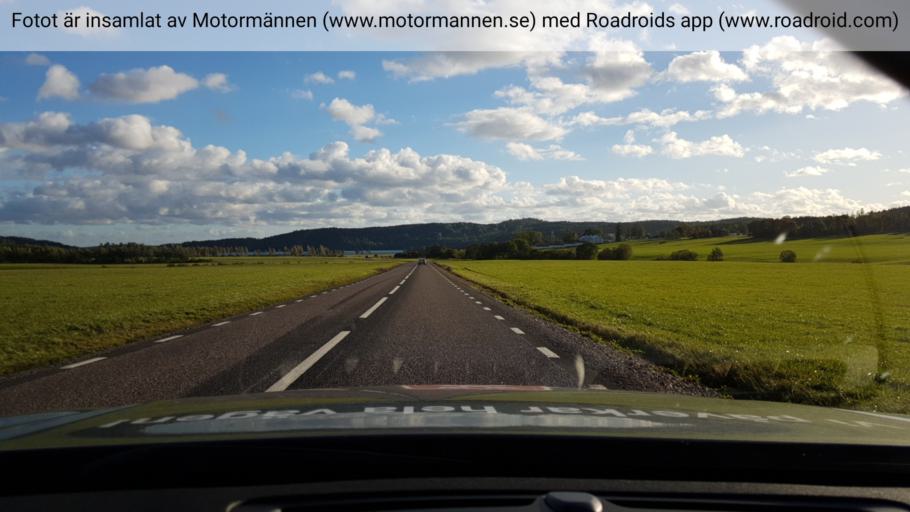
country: SE
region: Vaermland
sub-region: Karlstads Kommun
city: Molkom
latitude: 59.6894
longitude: 13.6811
